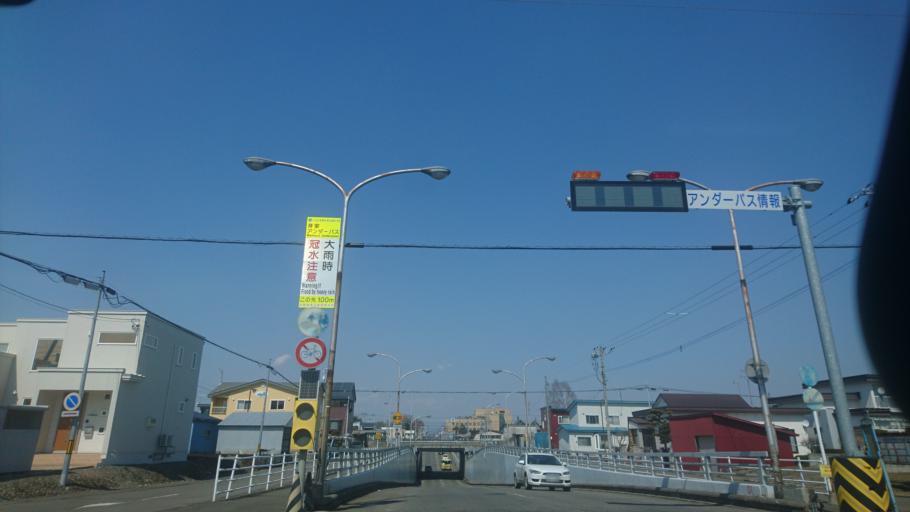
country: JP
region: Hokkaido
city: Obihiro
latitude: 42.9092
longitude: 143.0546
